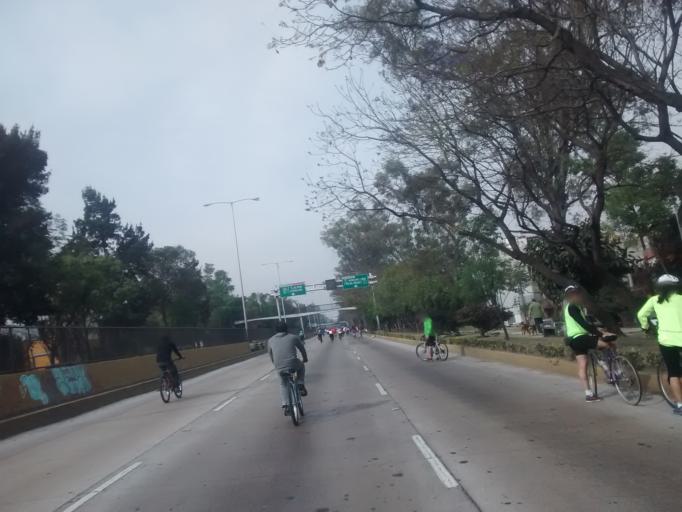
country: MX
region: Mexico City
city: Colonia Nativitas
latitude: 19.3699
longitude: -99.1142
